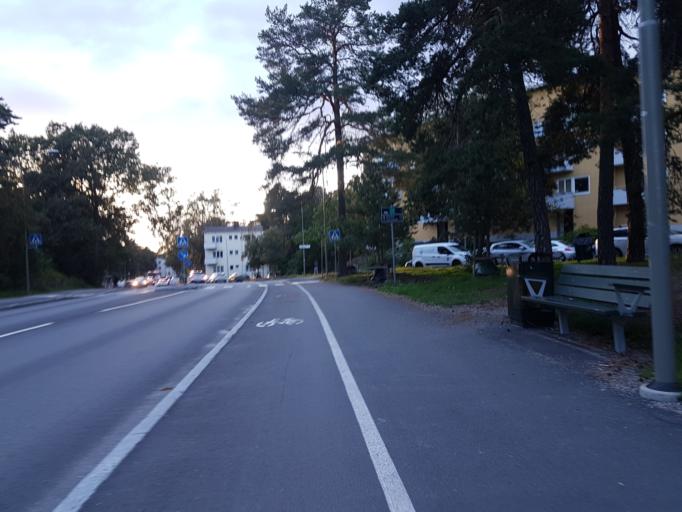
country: SE
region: Stockholm
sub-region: Stockholms Kommun
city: OEstermalm
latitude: 59.2965
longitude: 18.0954
